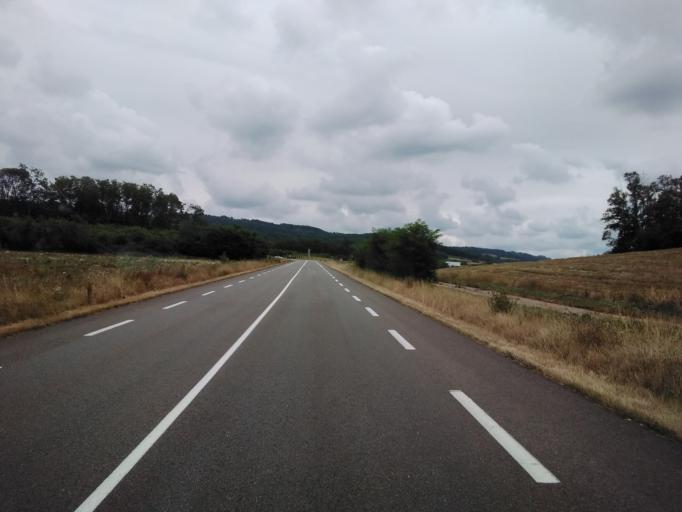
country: FR
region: Franche-Comte
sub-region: Departement du Jura
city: Montmorot
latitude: 46.6549
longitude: 5.5077
